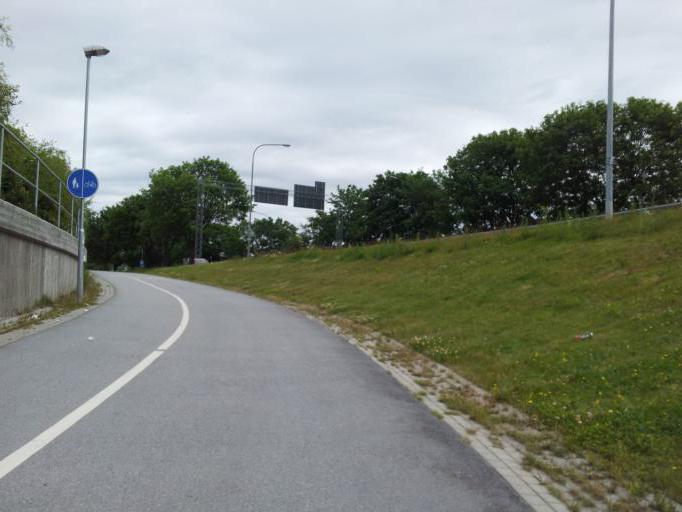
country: SE
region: Uppsala
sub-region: Uppsala Kommun
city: Uppsala
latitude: 59.8760
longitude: 17.6435
